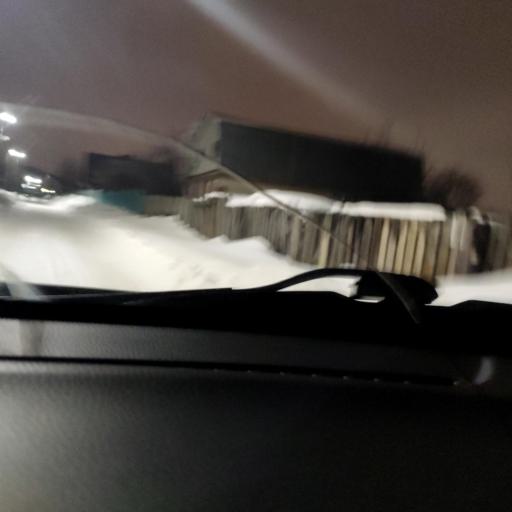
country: RU
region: Tatarstan
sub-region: Gorod Kazan'
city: Kazan
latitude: 55.7165
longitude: 49.0936
